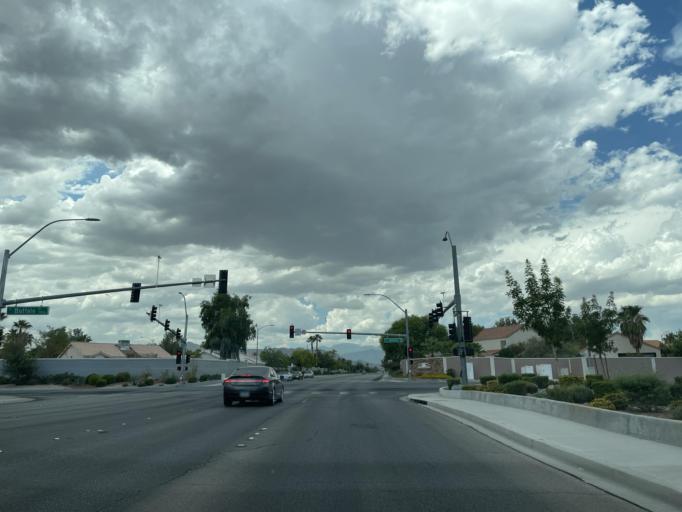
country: US
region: Nevada
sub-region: Clark County
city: North Las Vegas
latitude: 36.2979
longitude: -115.2596
